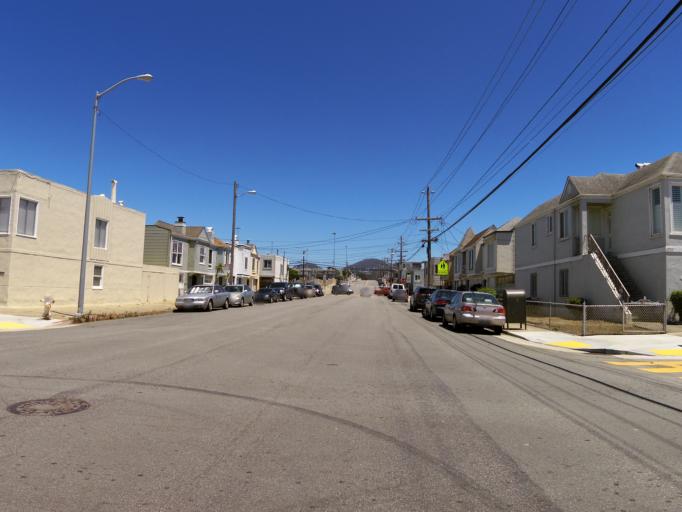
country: US
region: California
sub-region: San Mateo County
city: Daly City
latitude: 37.7363
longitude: -122.5011
